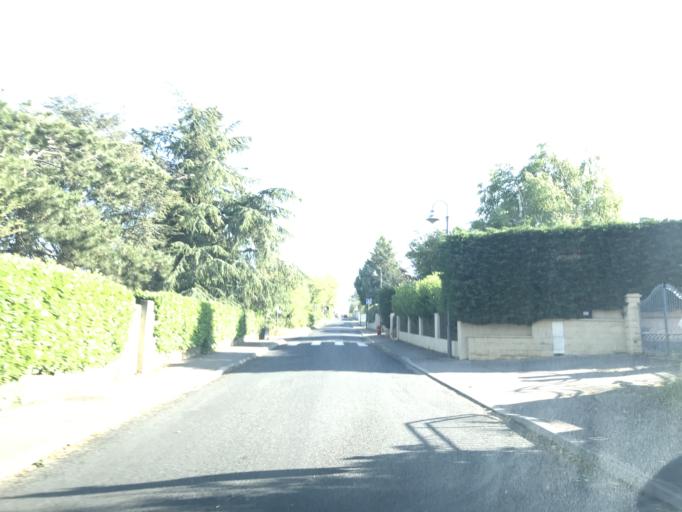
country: FR
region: Rhone-Alpes
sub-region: Departement du Rhone
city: Mions
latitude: 45.6578
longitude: 4.9577
